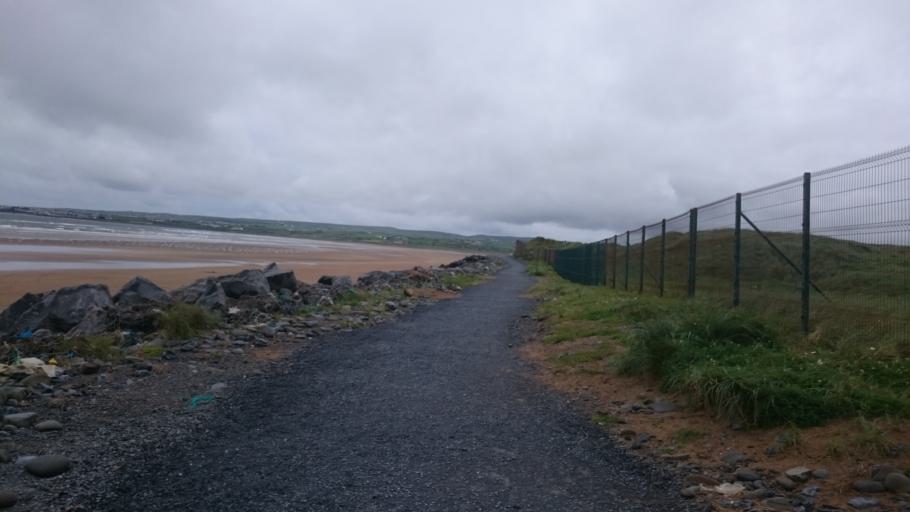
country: IE
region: Munster
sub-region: An Clar
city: Kilrush
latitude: 52.9362
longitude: -9.3516
